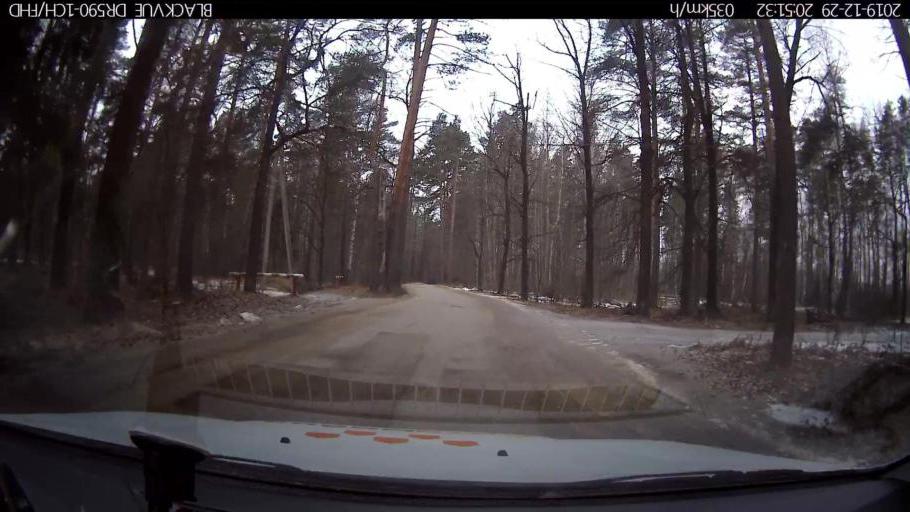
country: RU
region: Nizjnij Novgorod
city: Afonino
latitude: 56.1782
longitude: 44.0012
